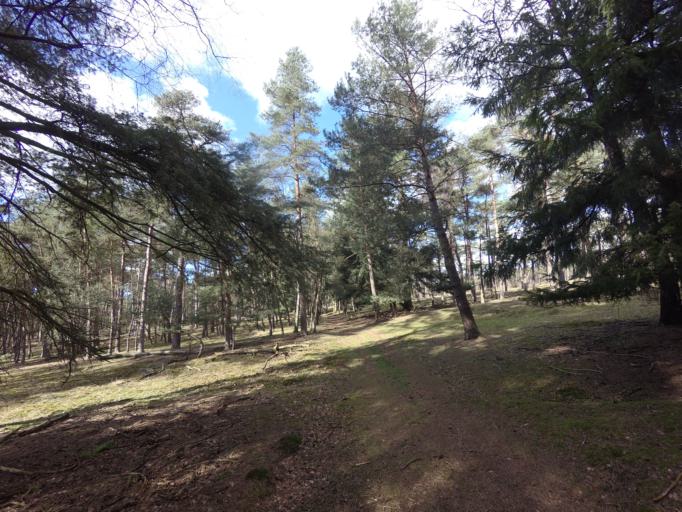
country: NL
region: Utrecht
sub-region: Gemeente Utrechtse Heuvelrug
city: Driebergen-Rijsenburg
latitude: 52.0753
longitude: 5.2809
